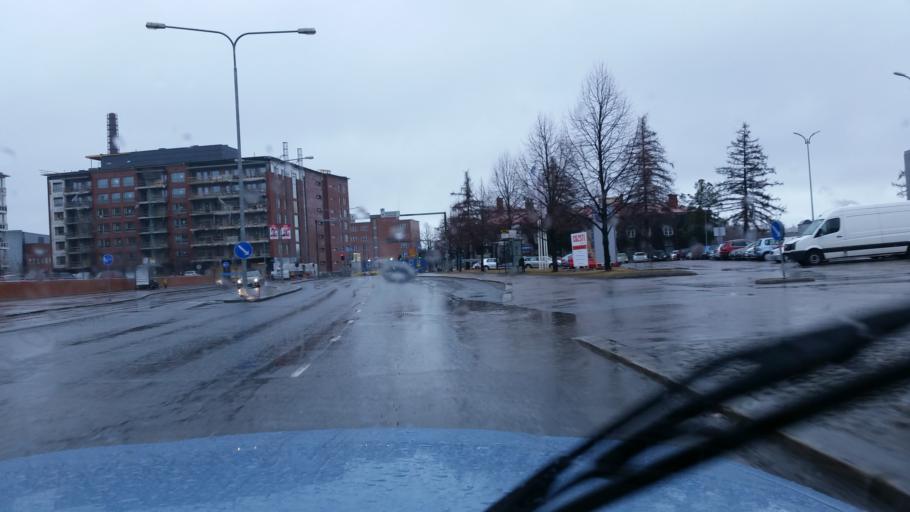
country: FI
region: Pirkanmaa
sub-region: Tampere
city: Tampere
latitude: 61.4824
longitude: 23.7631
